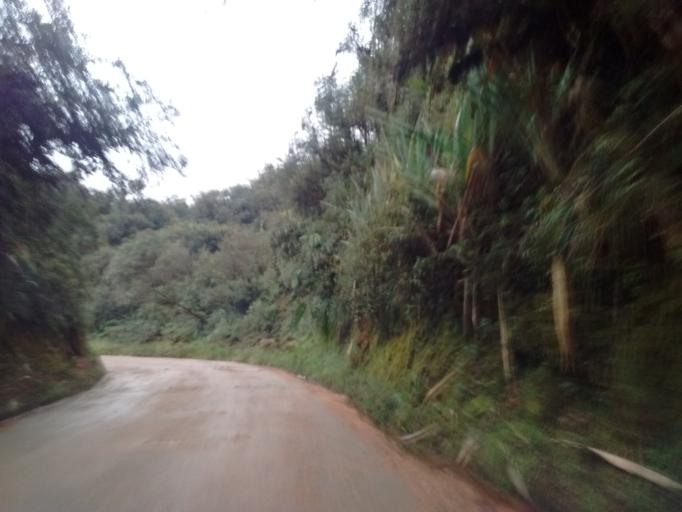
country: CO
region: Huila
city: Isnos
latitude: 2.1389
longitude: -76.3817
